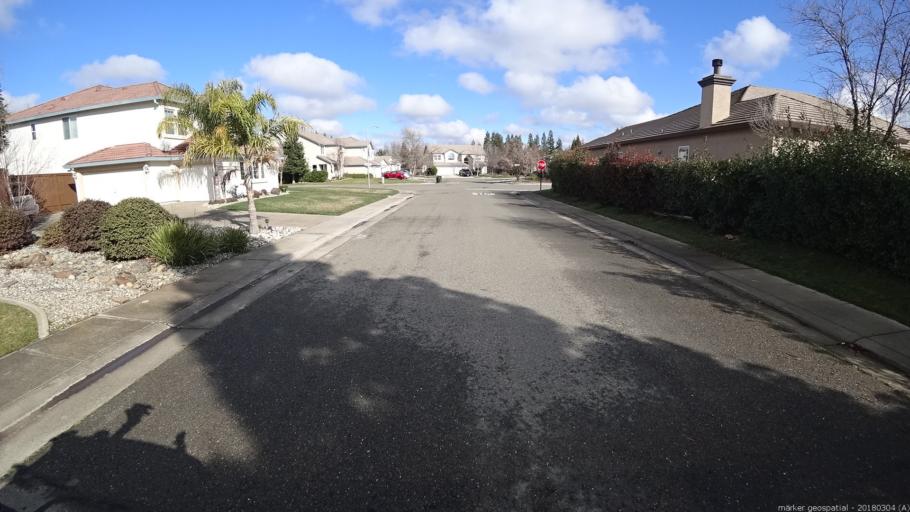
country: US
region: California
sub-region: Sacramento County
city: Vineyard
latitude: 38.4605
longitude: -121.3179
